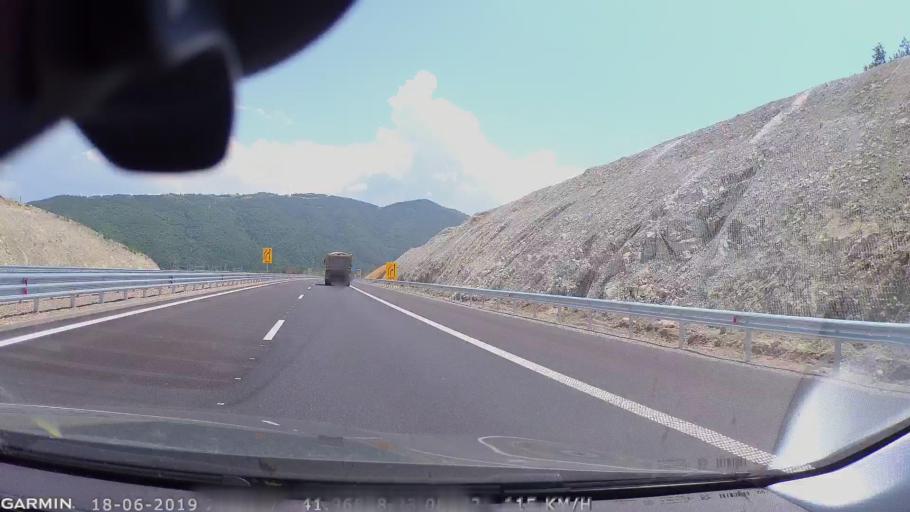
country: BG
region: Blagoevgrad
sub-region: Obshtina Blagoevgrad
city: Blagoevgrad
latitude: 41.9680
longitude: 23.0901
